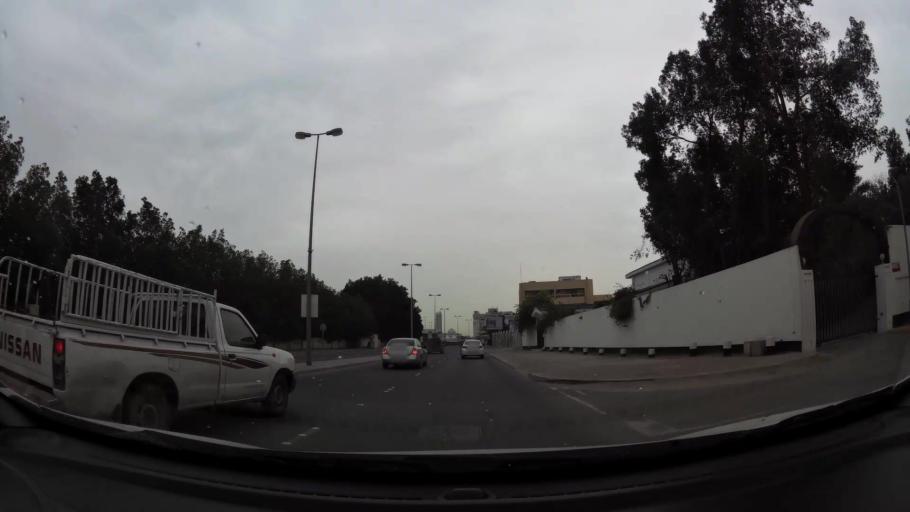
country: BH
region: Manama
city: Jidd Hafs
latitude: 26.2060
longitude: 50.5340
